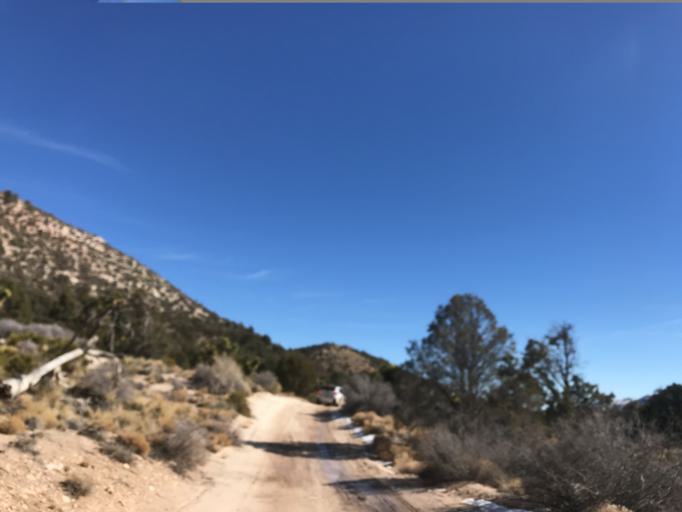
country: US
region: California
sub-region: San Bernardino County
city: Big Bear City
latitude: 34.2414
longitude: -116.6940
